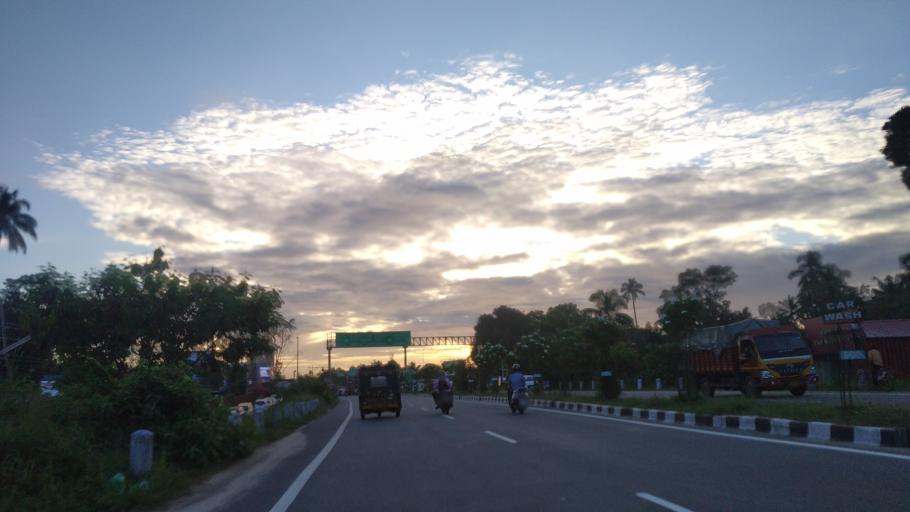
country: IN
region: Kerala
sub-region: Ernakulam
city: Elur
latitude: 10.0624
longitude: 76.2904
